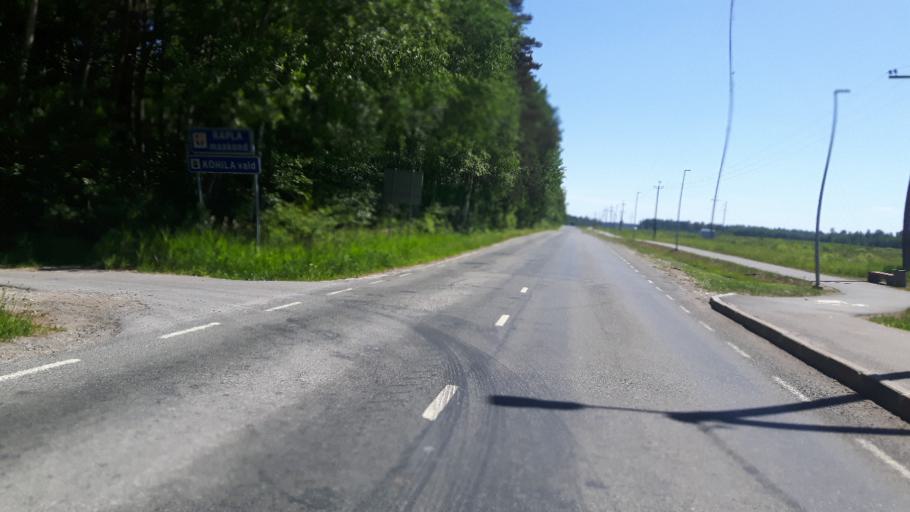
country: EE
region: Harju
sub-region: Saku vald
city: Saku
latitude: 59.2174
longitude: 24.6758
